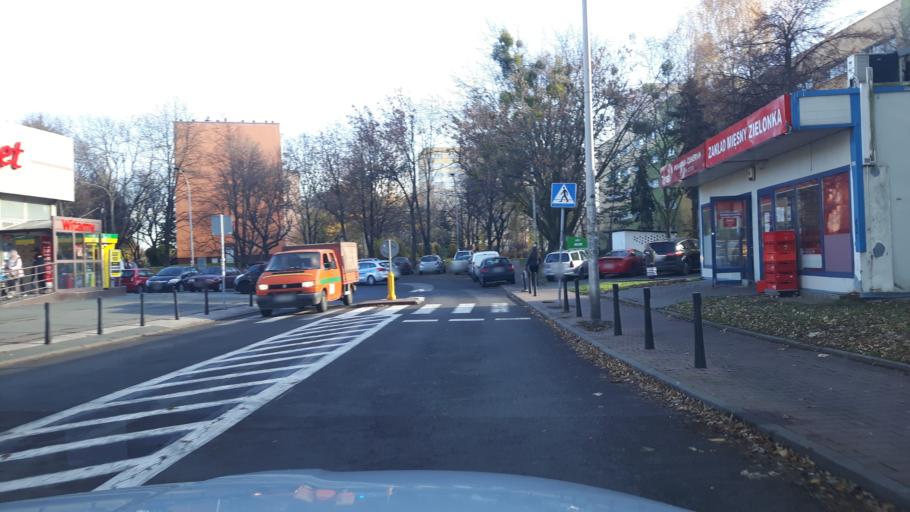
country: PL
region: Masovian Voivodeship
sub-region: Warszawa
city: Ochota
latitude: 52.2002
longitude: 20.9692
